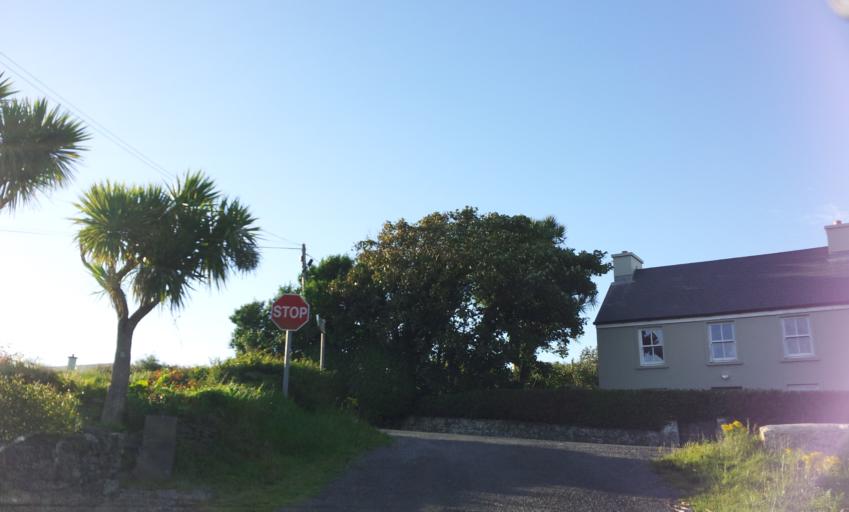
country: IE
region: Munster
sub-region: Ciarrai
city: Dingle
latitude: 52.1234
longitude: -10.3269
